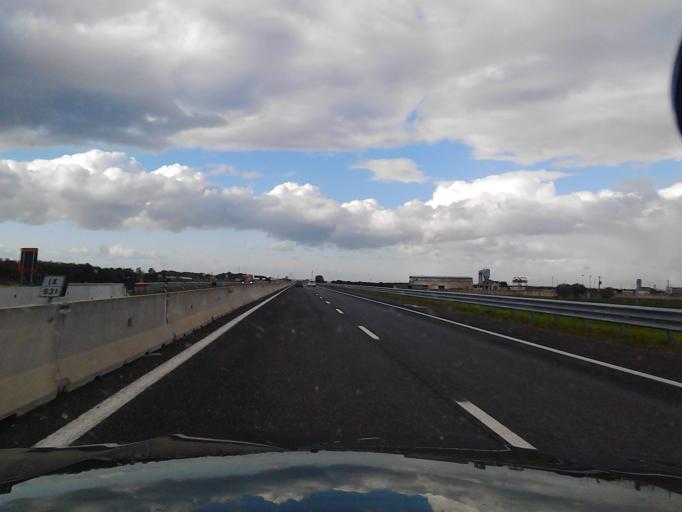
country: IT
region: Apulia
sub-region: Provincia di Barletta - Andria - Trani
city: Andria
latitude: 41.2455
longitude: 16.3492
